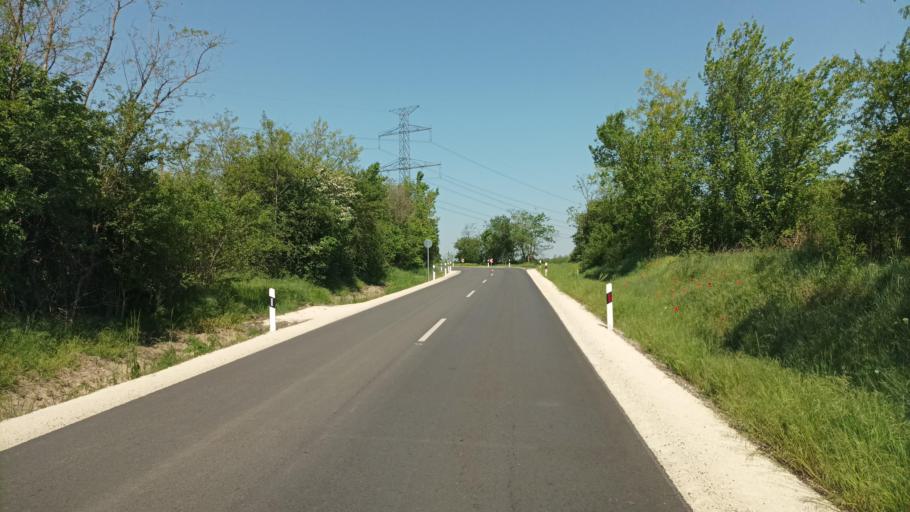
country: HU
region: Pest
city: Gomba
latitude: 47.3837
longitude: 19.5064
